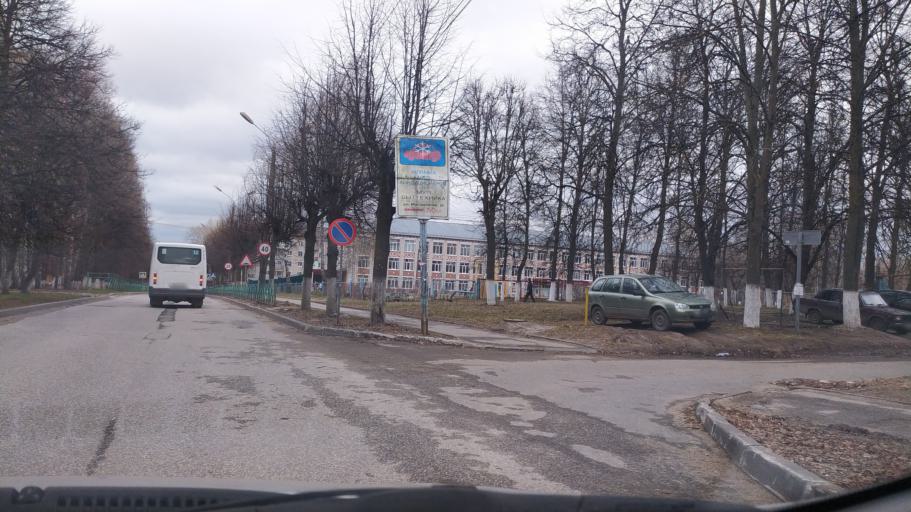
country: RU
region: Chuvashia
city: Novocheboksarsk
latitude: 56.1187
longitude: 47.4962
